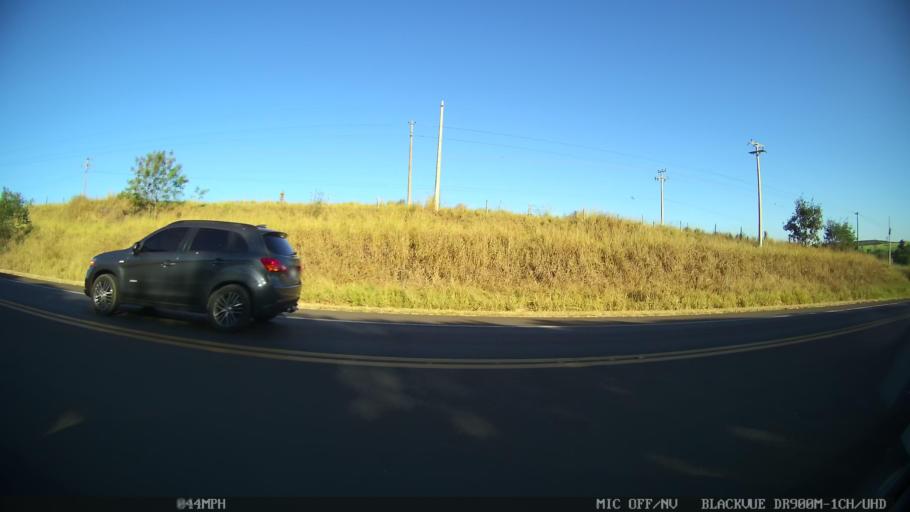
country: BR
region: Sao Paulo
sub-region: Olimpia
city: Olimpia
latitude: -20.6939
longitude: -48.9243
